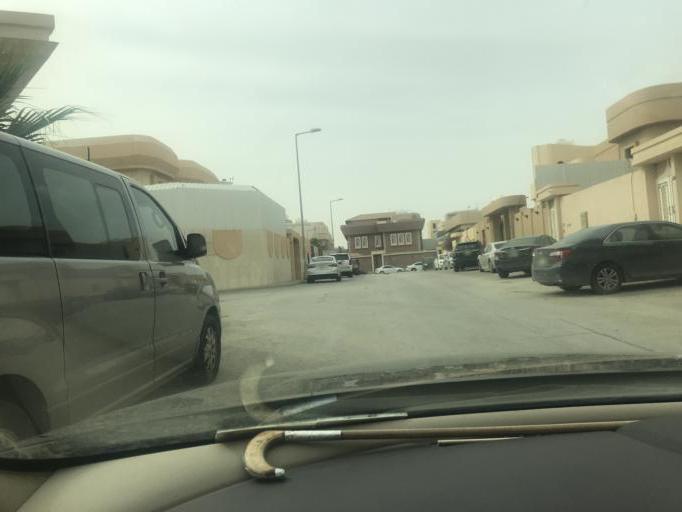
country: SA
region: Ar Riyad
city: Riyadh
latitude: 24.7508
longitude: 46.7620
